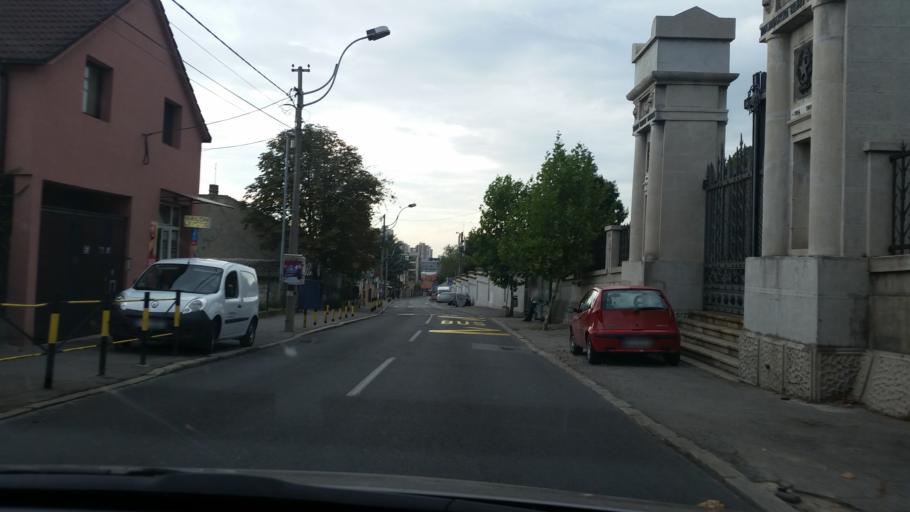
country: RS
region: Central Serbia
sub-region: Belgrade
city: Vracar
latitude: 44.8057
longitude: 20.4905
